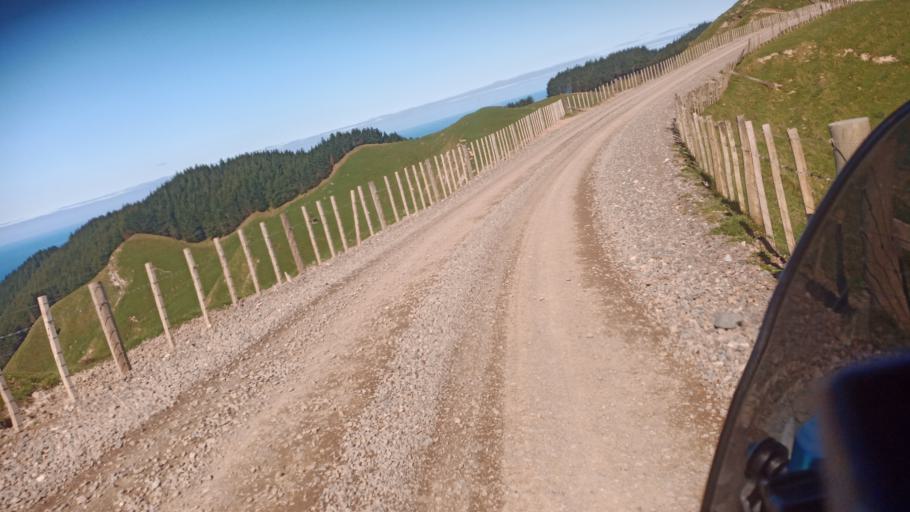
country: NZ
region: Gisborne
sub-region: Gisborne District
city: Gisborne
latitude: -39.1684
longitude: 177.8990
